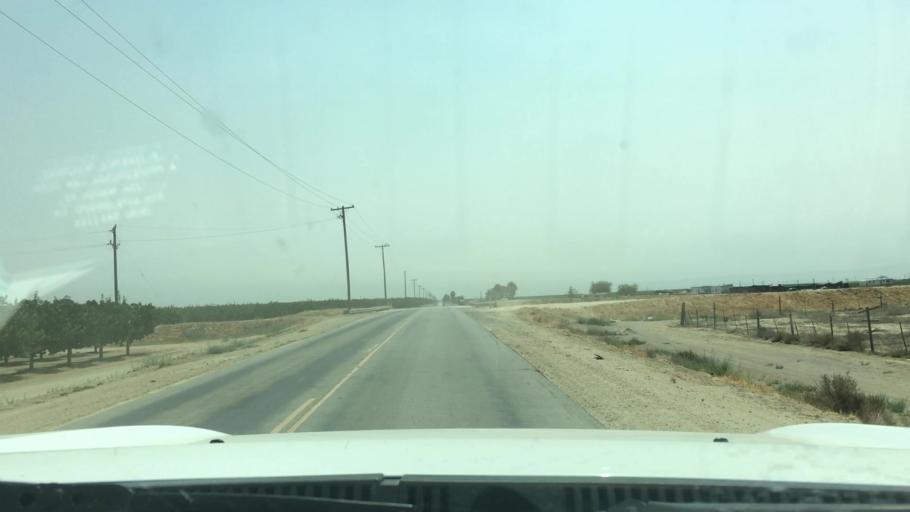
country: US
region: California
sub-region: Kern County
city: Wasco
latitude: 35.6820
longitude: -119.4374
